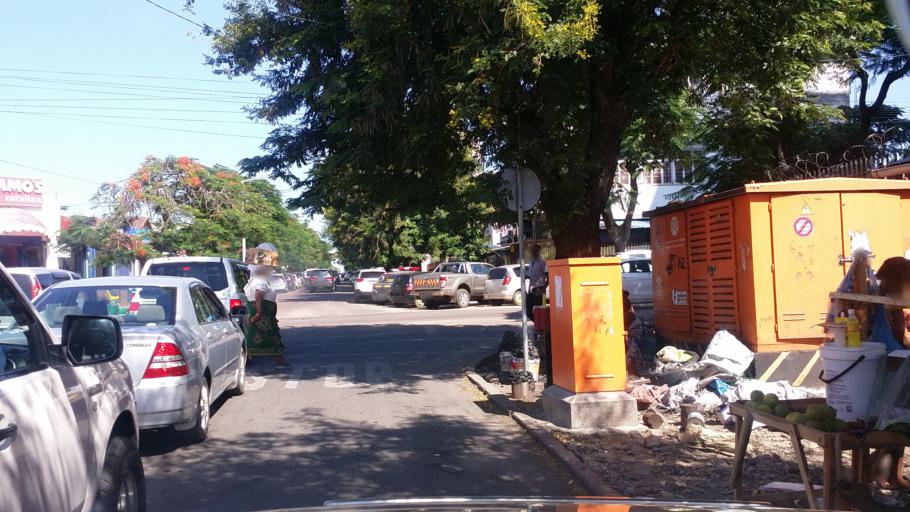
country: MZ
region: Maputo City
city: Maputo
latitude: -25.9624
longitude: 32.5815
